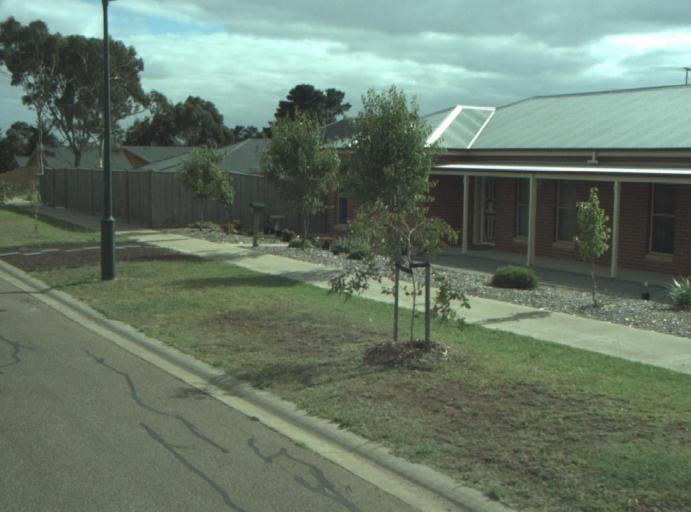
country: AU
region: Victoria
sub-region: Greater Geelong
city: Wandana Heights
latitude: -38.2106
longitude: 144.2988
